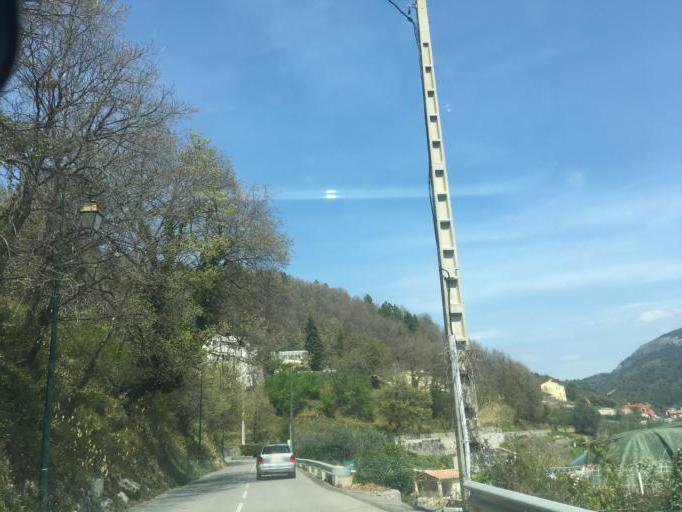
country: FR
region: Provence-Alpes-Cote d'Azur
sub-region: Departement des Alpes-Maritimes
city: Levens
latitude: 43.8466
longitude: 7.2198
